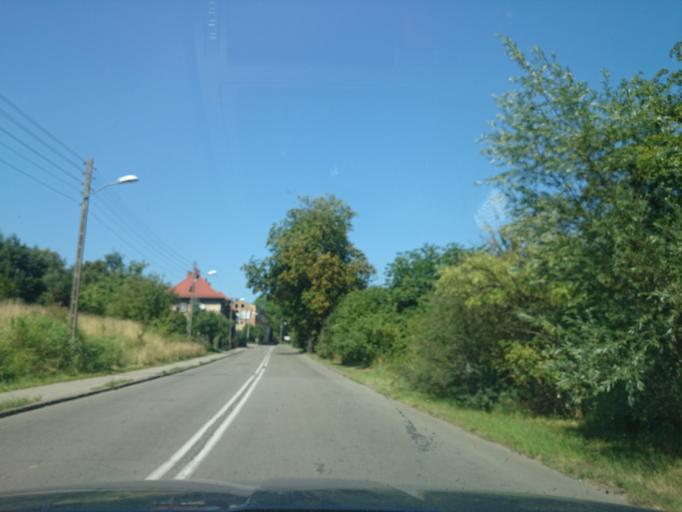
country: PL
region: West Pomeranian Voivodeship
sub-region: Powiat policki
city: Police
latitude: 53.4852
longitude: 14.6114
